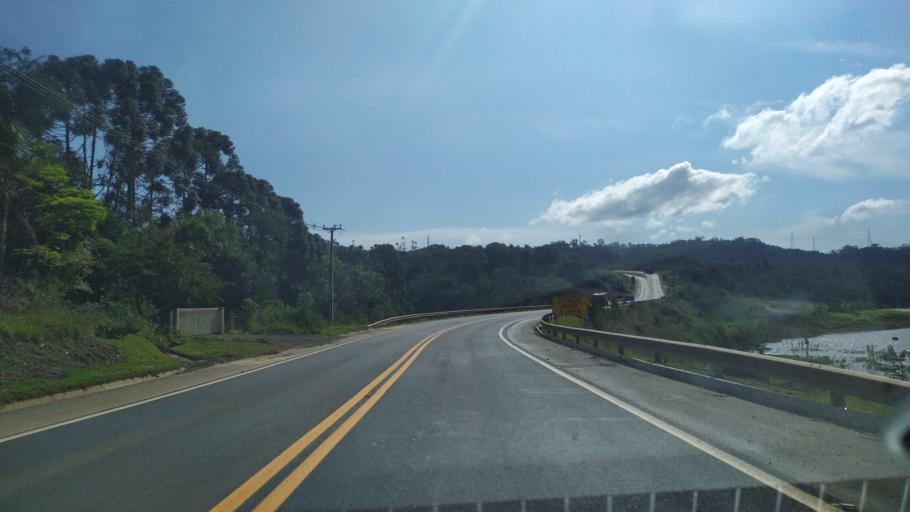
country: BR
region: Parana
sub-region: Telemaco Borba
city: Telemaco Borba
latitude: -24.2666
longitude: -50.7229
